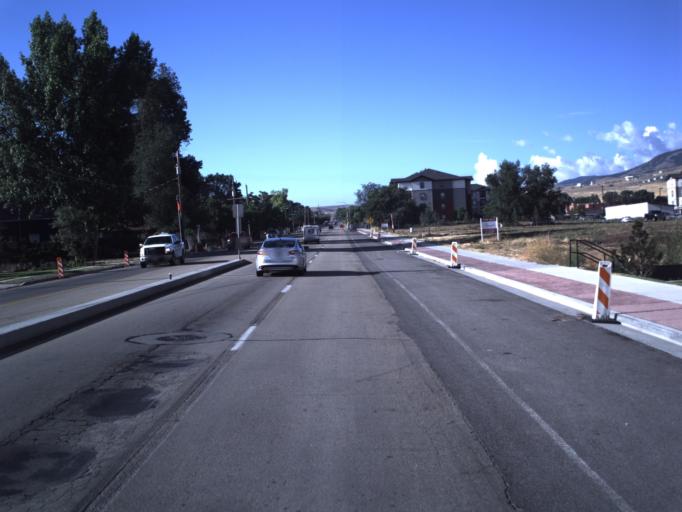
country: US
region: Utah
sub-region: Salt Lake County
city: Magna
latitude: 40.7103
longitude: -112.0919
